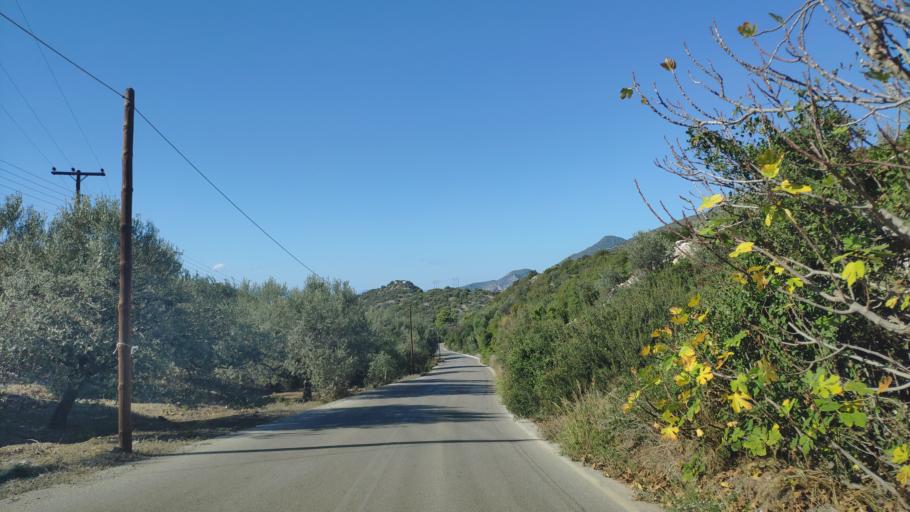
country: GR
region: Attica
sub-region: Nomos Piraios
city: Galatas
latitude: 37.5487
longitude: 23.3742
